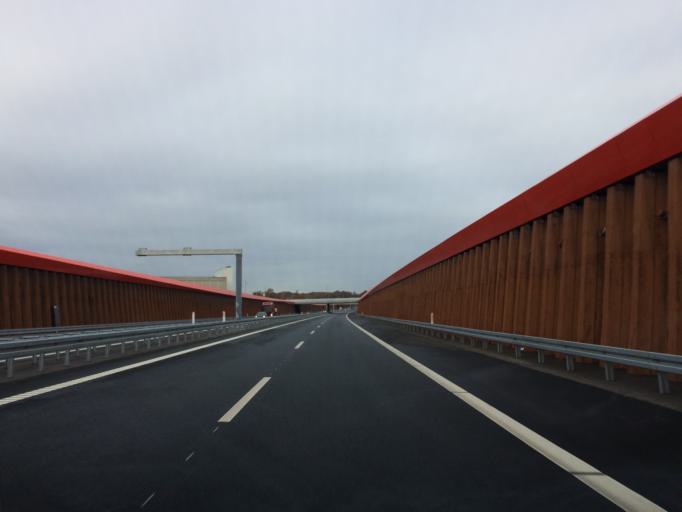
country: DK
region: Central Jutland
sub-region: Silkeborg Kommune
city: Silkeborg
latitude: 56.1853
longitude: 9.5782
